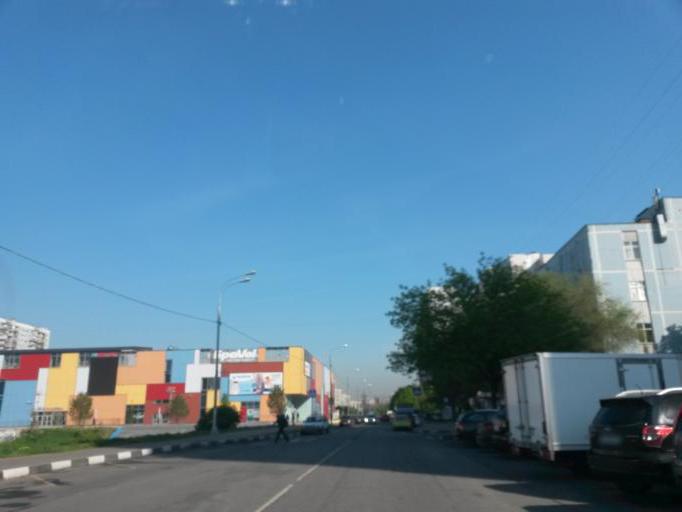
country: RU
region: Moscow
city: Brateyevo
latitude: 55.6380
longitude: 37.7613
